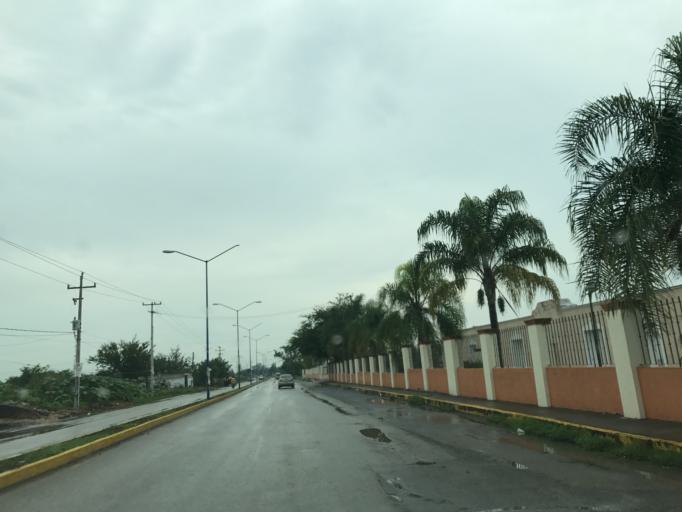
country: MX
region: Morelos
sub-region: Ayala
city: Olintepec
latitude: 18.7536
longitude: -98.9851
